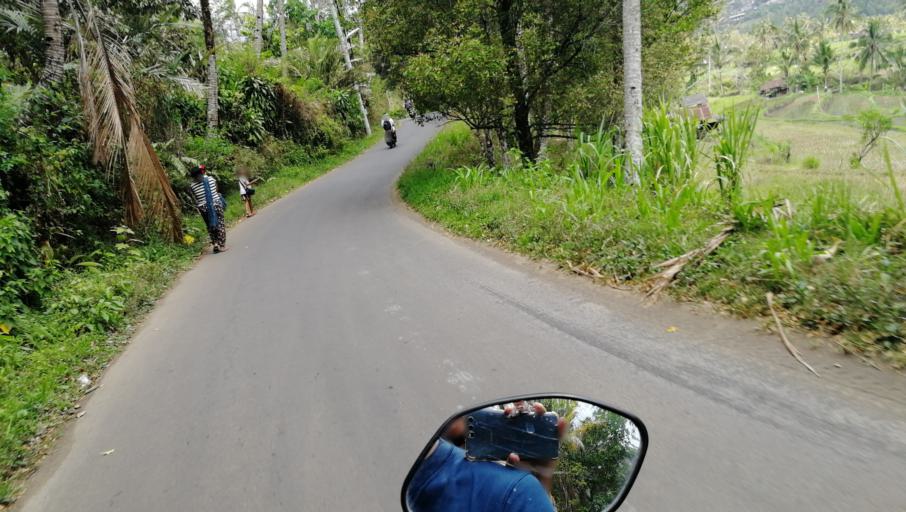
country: ID
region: Bali
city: Munduk
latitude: -8.2657
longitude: 115.0450
